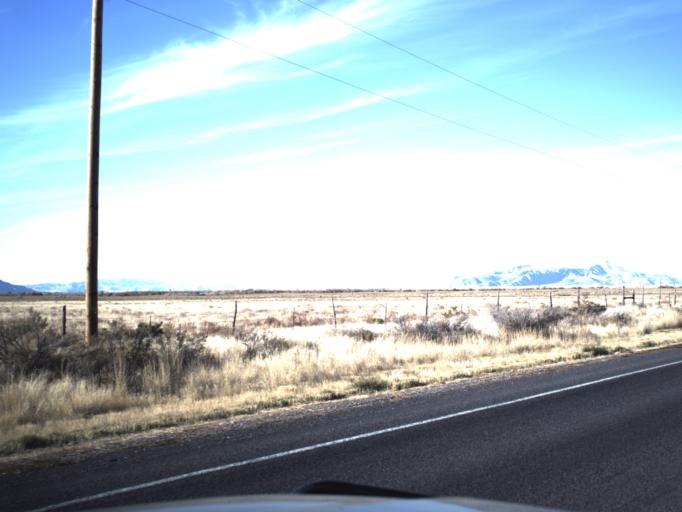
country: US
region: Utah
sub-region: Tooele County
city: Erda
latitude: 40.6107
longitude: -112.3709
